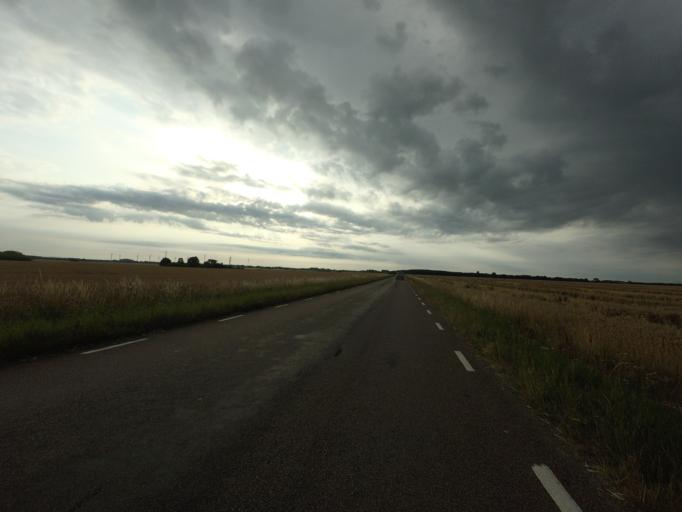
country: SE
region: Skane
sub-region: Helsingborg
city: Odakra
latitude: 56.1562
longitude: 12.7111
